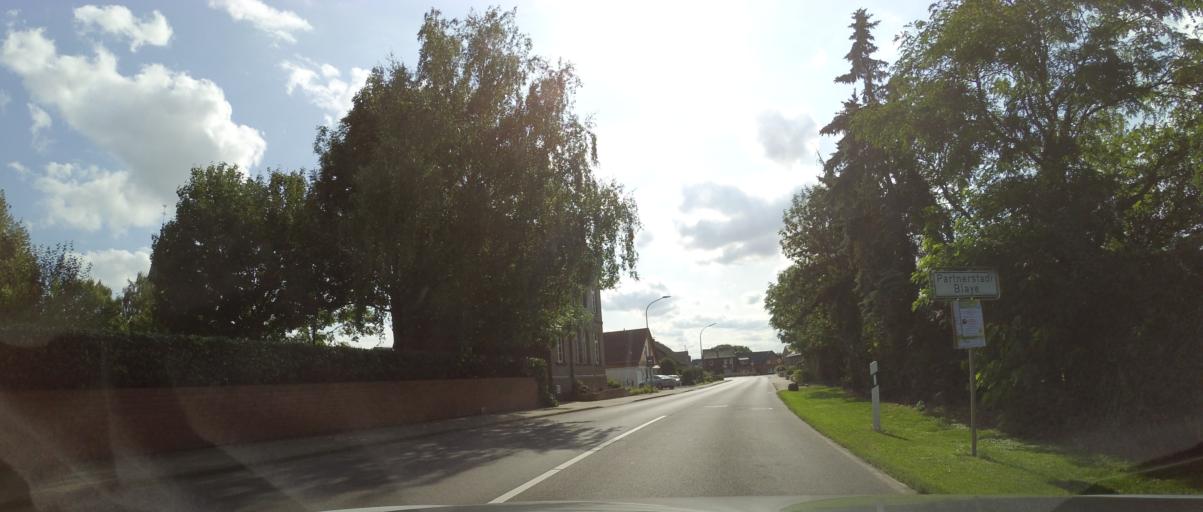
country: DE
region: North Rhine-Westphalia
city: Zulpich
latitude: 50.7453
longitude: 6.7071
